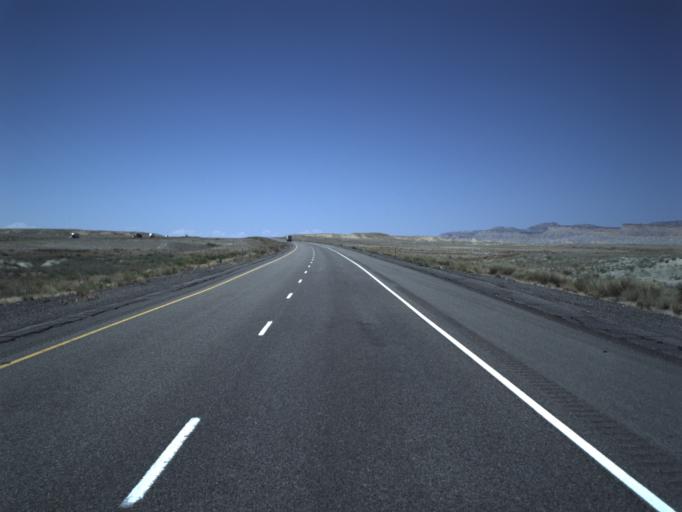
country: US
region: Utah
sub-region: Grand County
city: Moab
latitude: 38.9423
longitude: -109.5250
